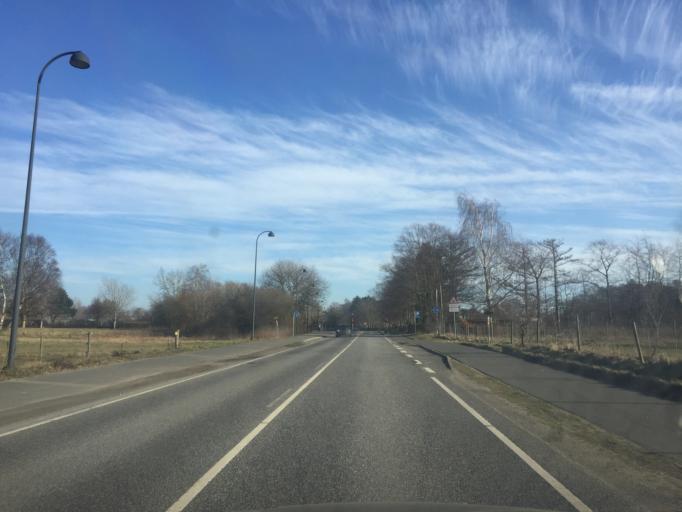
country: DK
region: Capital Region
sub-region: Rudersdal Kommune
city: Trorod
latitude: 55.8503
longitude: 12.5567
